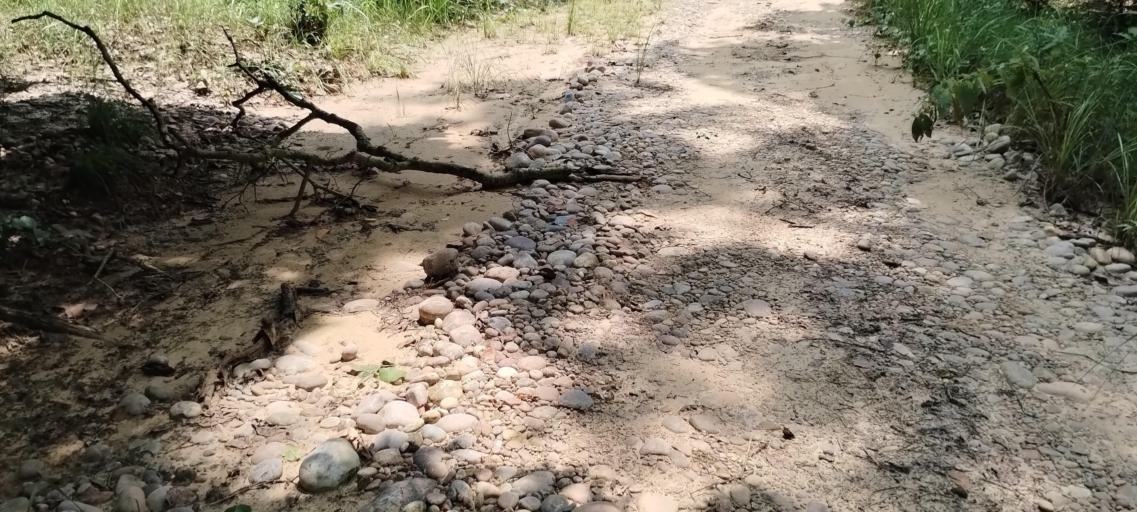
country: NP
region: Far Western
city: Tikapur
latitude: 28.4984
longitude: 81.2560
